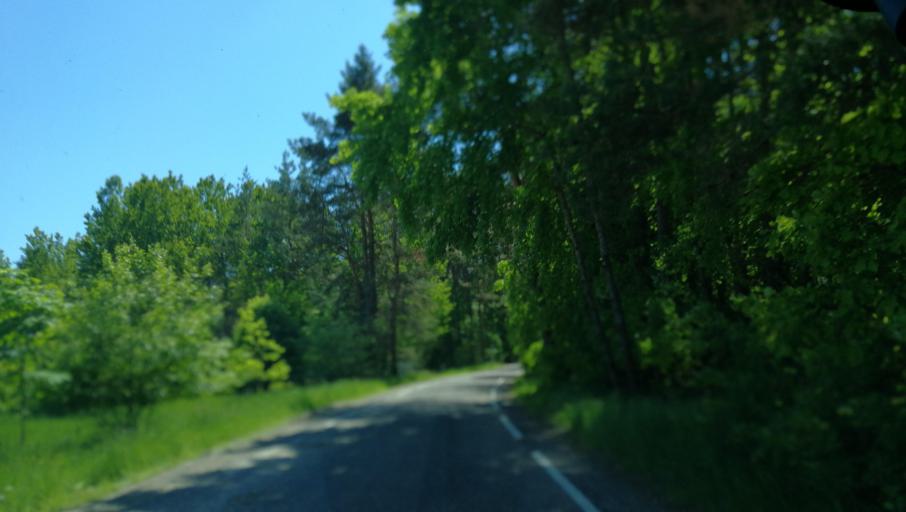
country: LV
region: Kekava
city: Kekava
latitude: 56.8637
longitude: 24.2441
